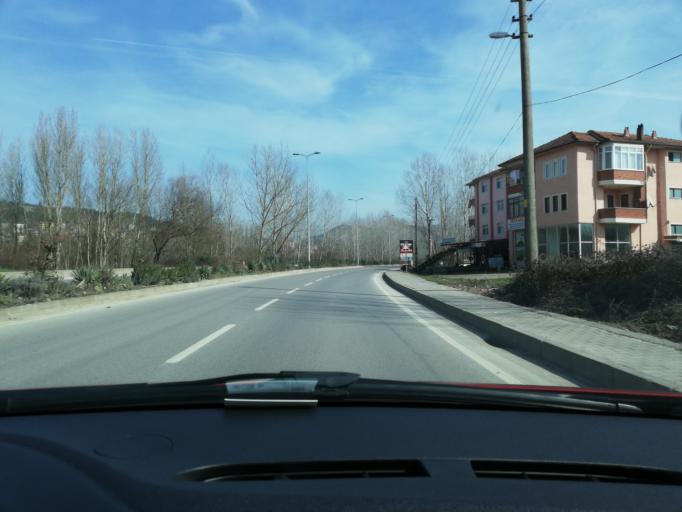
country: TR
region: Bartin
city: Bartin
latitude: 41.6359
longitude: 32.3491
